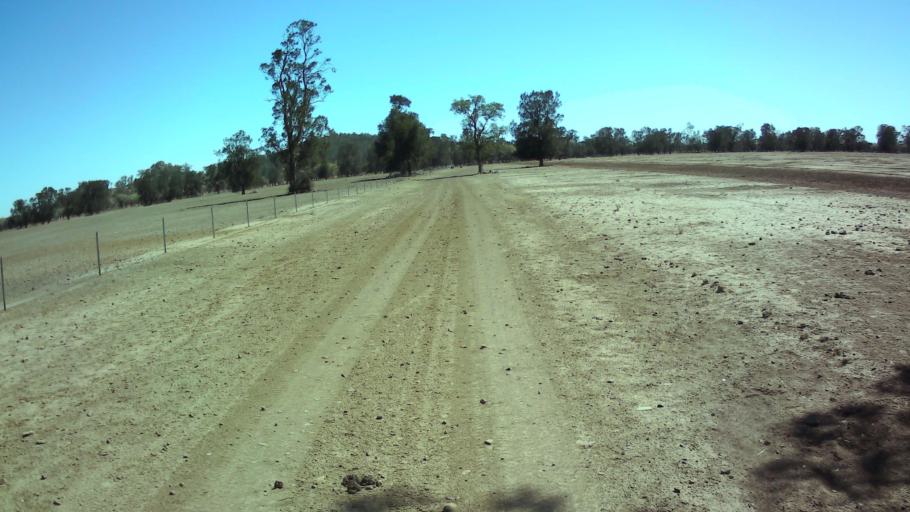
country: AU
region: New South Wales
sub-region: Bland
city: West Wyalong
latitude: -33.7439
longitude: 147.6612
